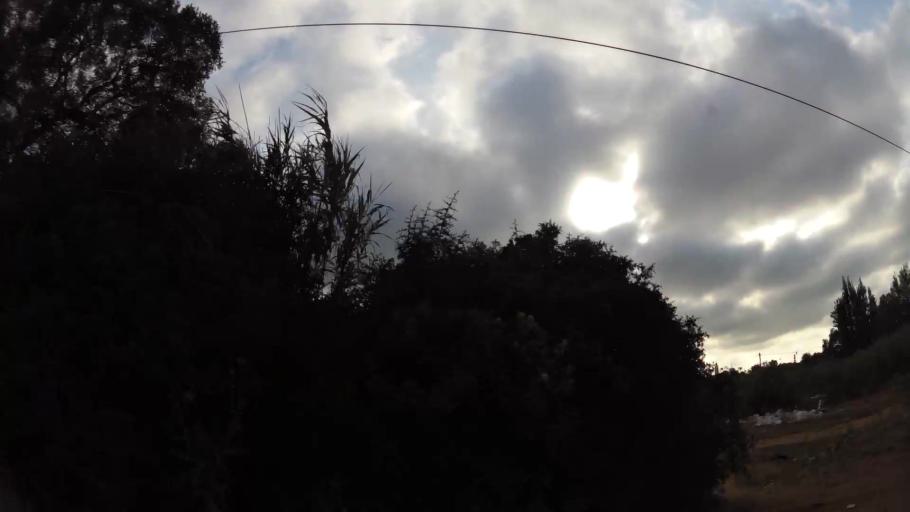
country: MA
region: Rabat-Sale-Zemmour-Zaer
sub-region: Skhirate-Temara
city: Temara
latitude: 33.9494
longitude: -6.8486
